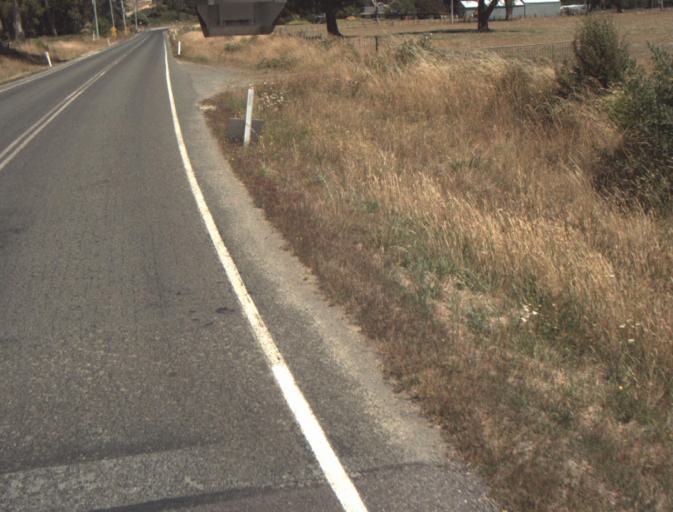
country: AU
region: Tasmania
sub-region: Launceston
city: Newstead
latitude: -41.3226
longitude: 147.3627
